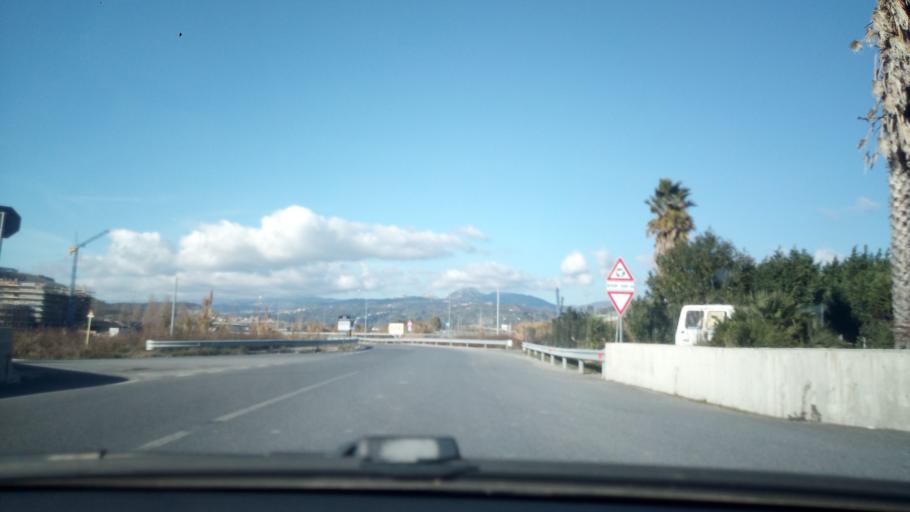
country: IT
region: Calabria
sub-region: Provincia di Catanzaro
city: Catanzaro
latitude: 38.8619
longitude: 16.5674
